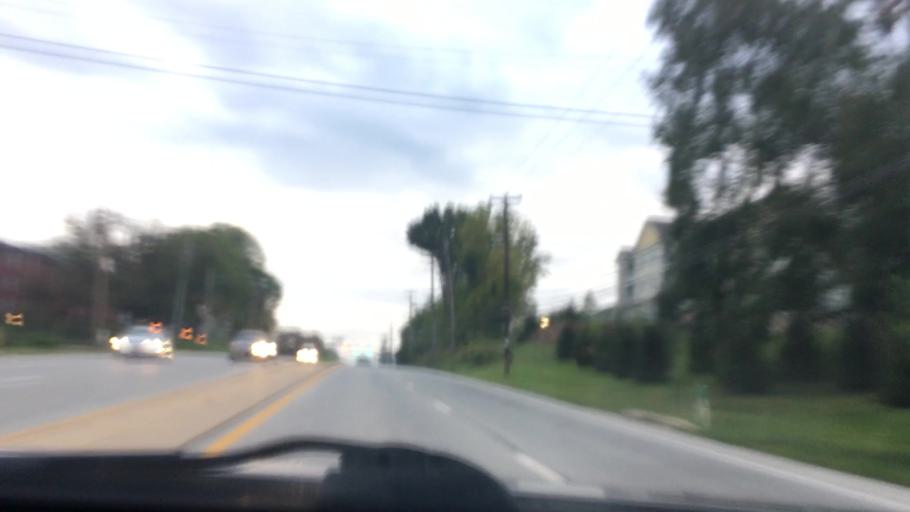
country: US
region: Pennsylvania
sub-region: Chester County
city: West Chester
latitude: 39.9660
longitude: -75.5473
